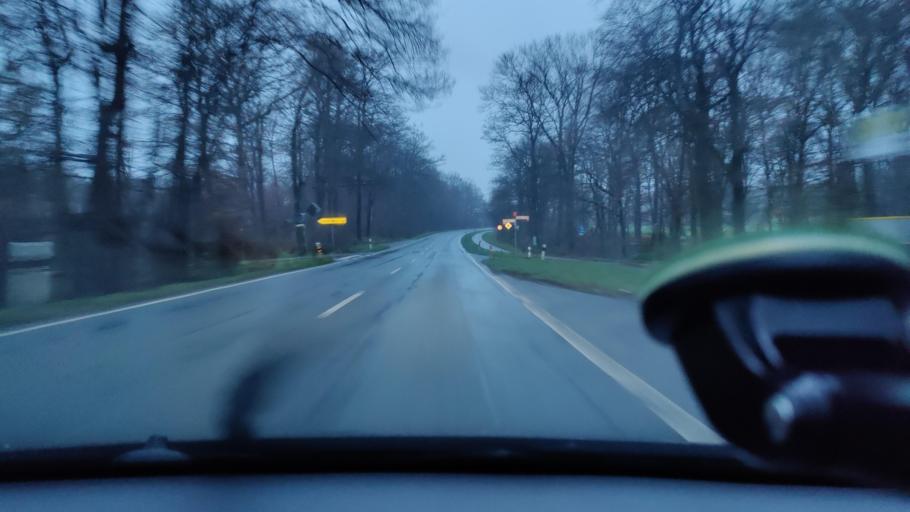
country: DE
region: North Rhine-Westphalia
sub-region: Regierungsbezirk Dusseldorf
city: Sonsbeck
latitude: 51.5851
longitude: 6.3857
